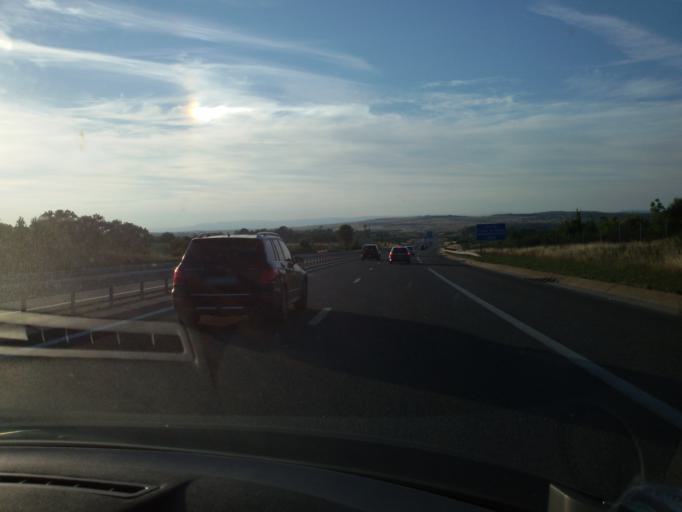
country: FR
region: Midi-Pyrenees
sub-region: Departement de l'Aveyron
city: La Cavalerie
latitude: 44.0032
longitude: 3.1519
